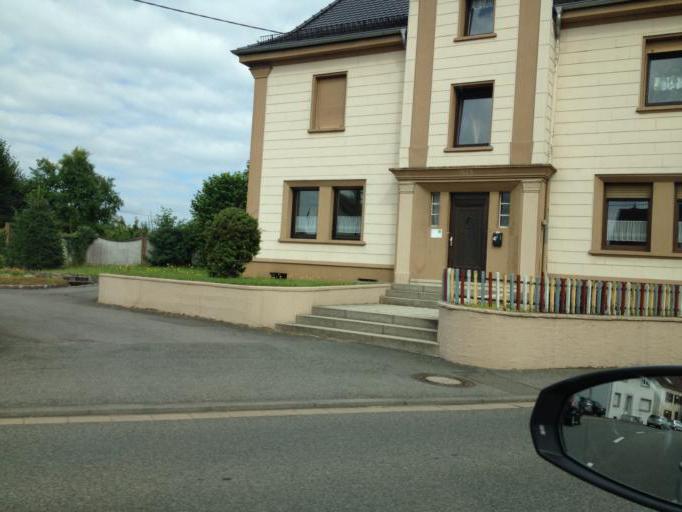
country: DE
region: Saarland
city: Losheim
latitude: 49.5100
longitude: 6.7427
